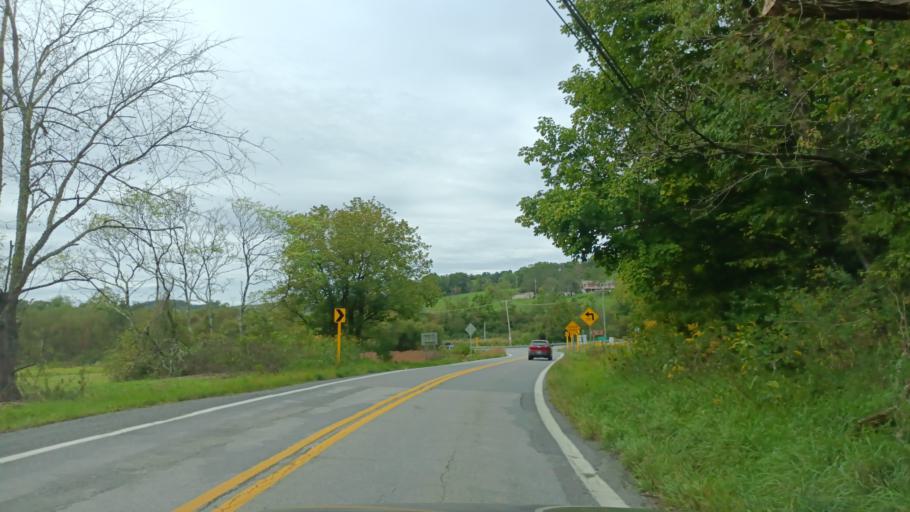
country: US
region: West Virginia
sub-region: Taylor County
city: Grafton
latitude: 39.3374
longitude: -79.8544
